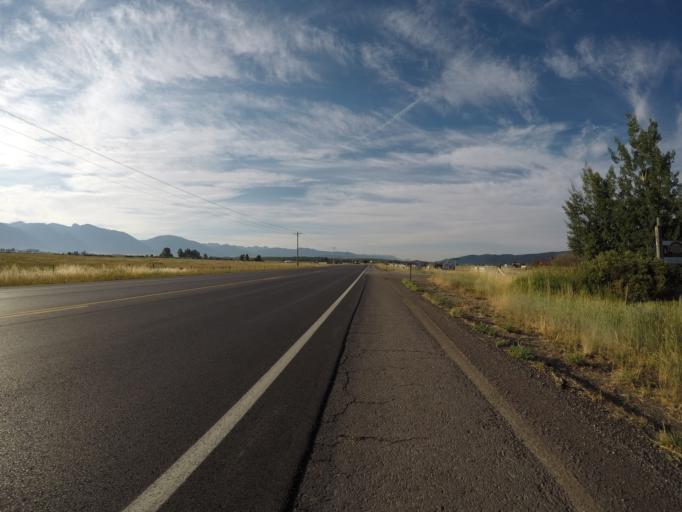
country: US
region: Wyoming
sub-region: Lincoln County
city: Afton
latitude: 42.9499
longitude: -111.0108
